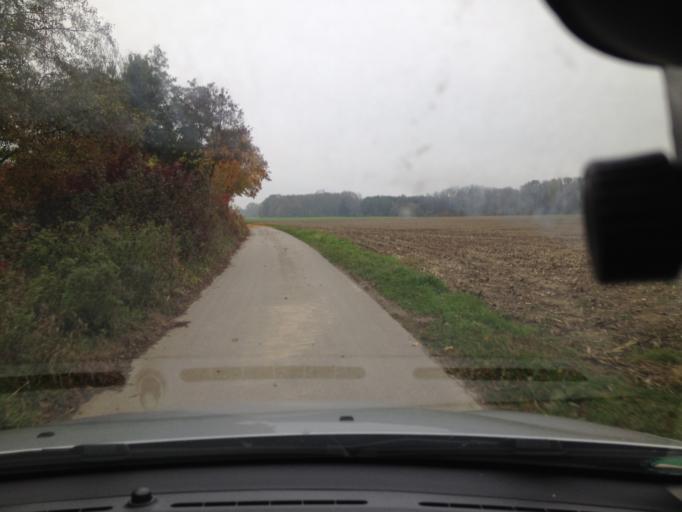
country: DE
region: Bavaria
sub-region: Swabia
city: Ettringen
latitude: 48.1364
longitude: 10.6754
